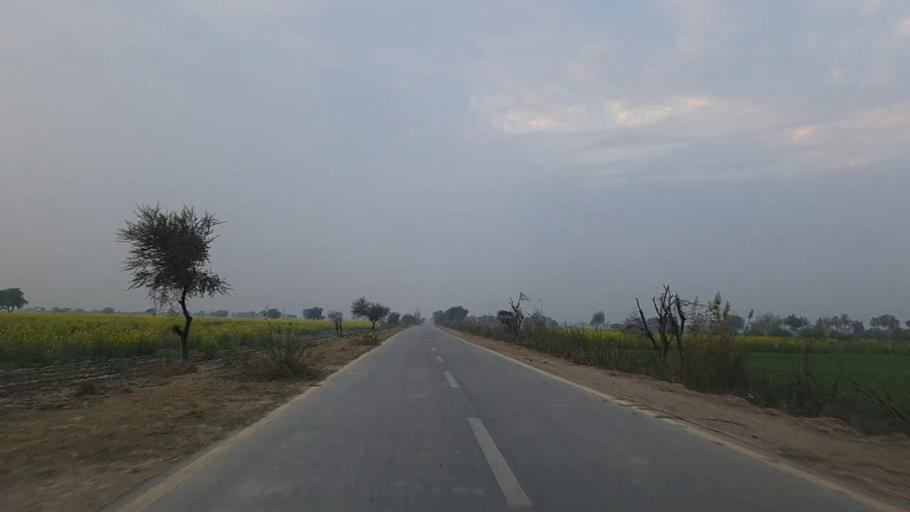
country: PK
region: Sindh
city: Jam Sahib
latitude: 26.3153
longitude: 68.5731
